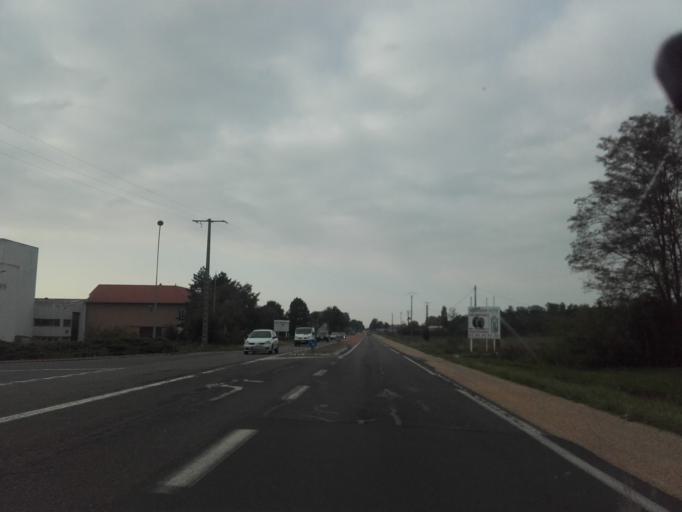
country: FR
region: Bourgogne
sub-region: Departement de Saone-et-Loire
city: Creches-sur-Saone
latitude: 46.2246
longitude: 4.7836
